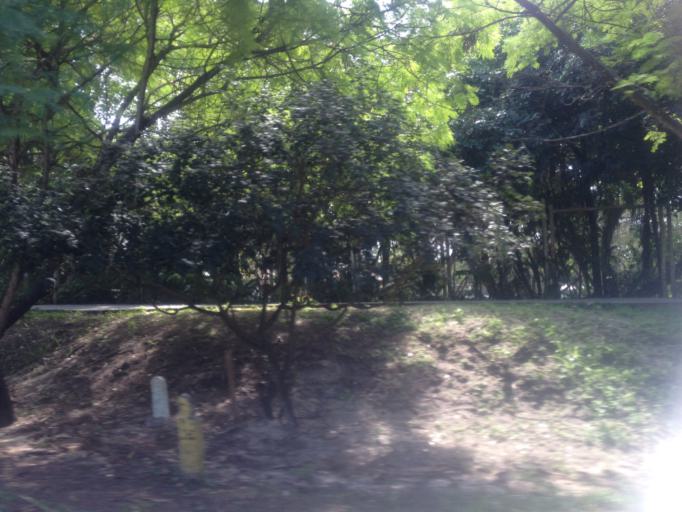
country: BR
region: Bahia
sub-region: Mata De Sao Joao
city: Mata de Sao Joao
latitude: -12.5770
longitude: -38.0163
